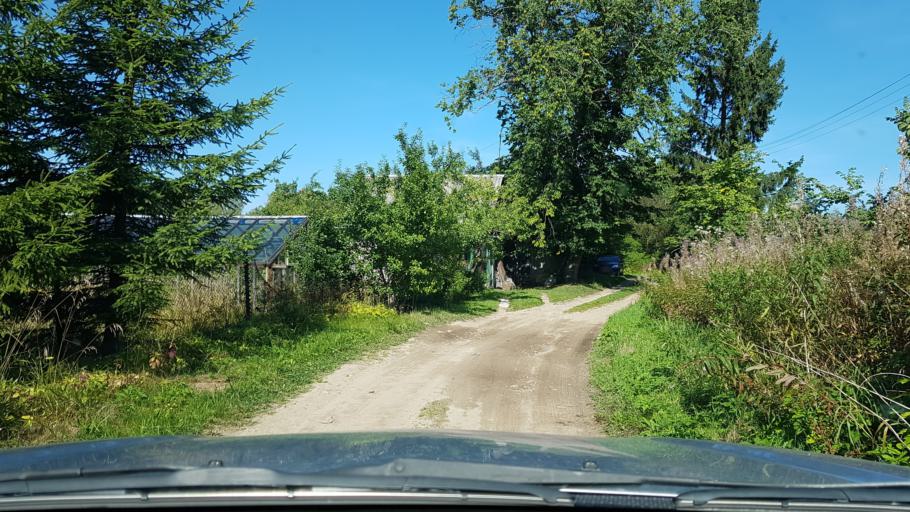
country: EE
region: Ida-Virumaa
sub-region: Sillamaee linn
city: Sillamae
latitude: 59.3249
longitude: 27.7760
